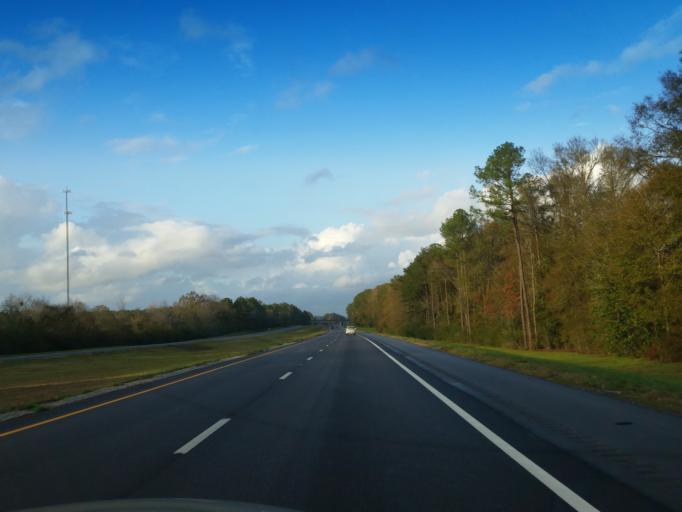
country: US
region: Mississippi
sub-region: Jones County
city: Sharon
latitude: 31.8277
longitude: -89.0506
